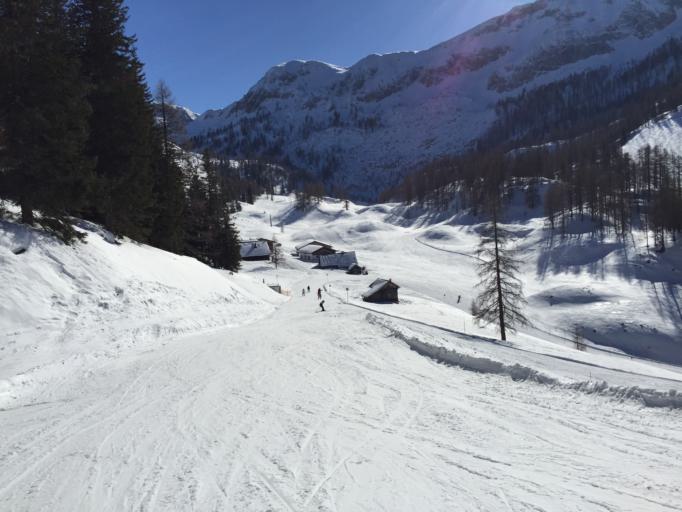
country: AT
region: Salzburg
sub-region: Politischer Bezirk Sankt Johann im Pongau
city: Untertauern
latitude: 47.2831
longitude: 13.4654
